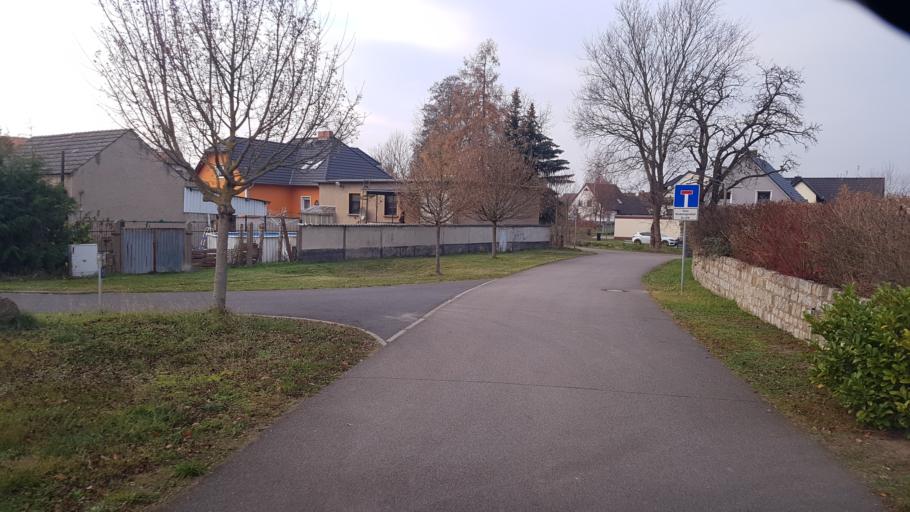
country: DE
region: Brandenburg
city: Ziltendorf
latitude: 52.2036
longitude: 14.6312
